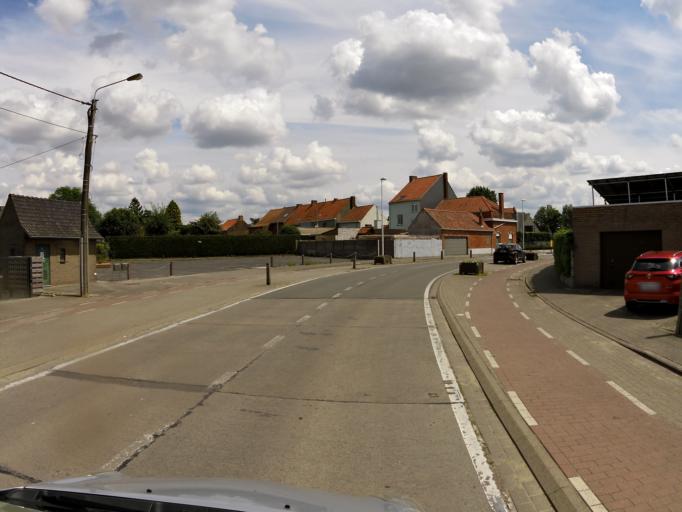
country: BE
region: Flanders
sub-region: Provincie West-Vlaanderen
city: Ieper
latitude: 50.8604
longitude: 2.9120
